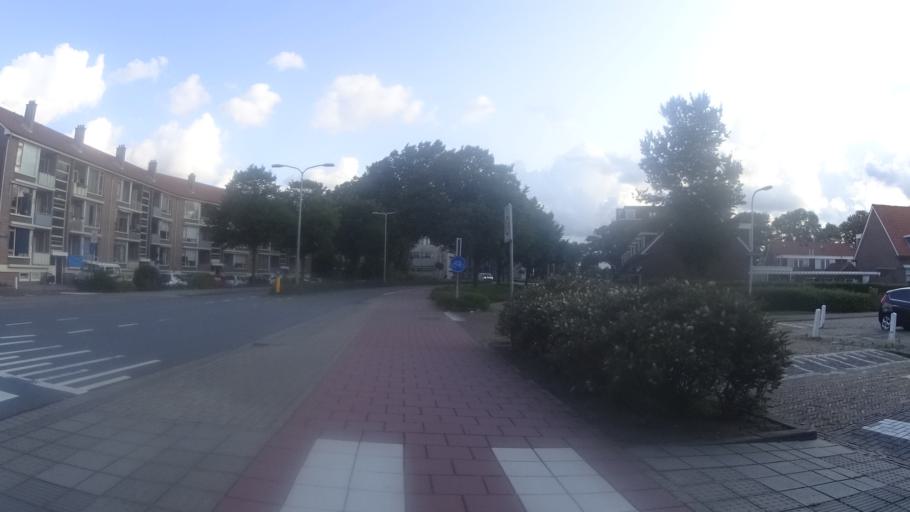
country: NL
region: South Holland
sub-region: Gemeente Katwijk
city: Katwijk aan Zee
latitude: 52.2037
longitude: 4.4088
